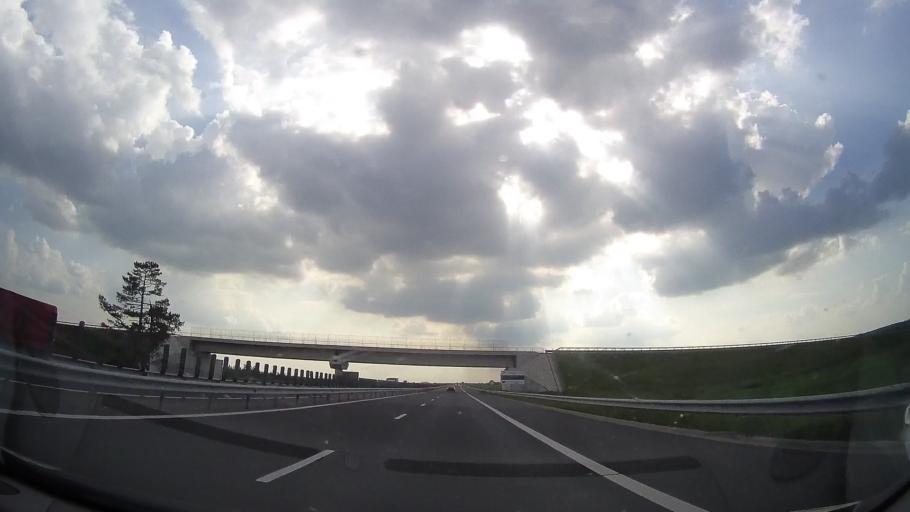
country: RO
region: Timis
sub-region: Comuna Balint
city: Balint
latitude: 45.8045
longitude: 21.9019
